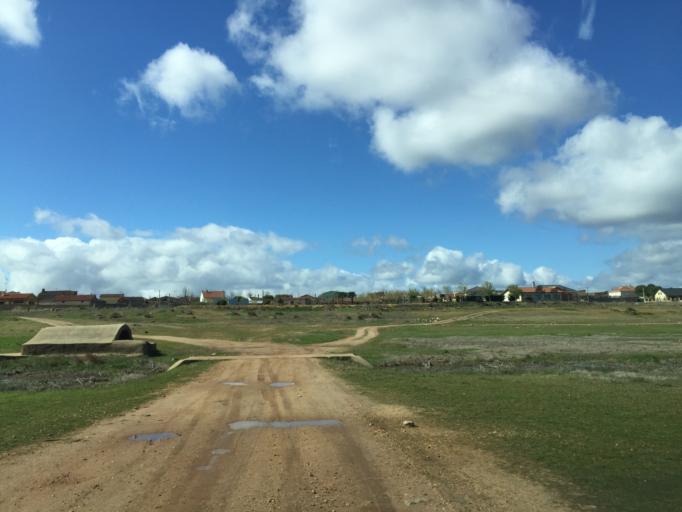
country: ES
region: Castille and Leon
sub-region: Provincia de Zamora
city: Montamarta
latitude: 41.6523
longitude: -5.8073
